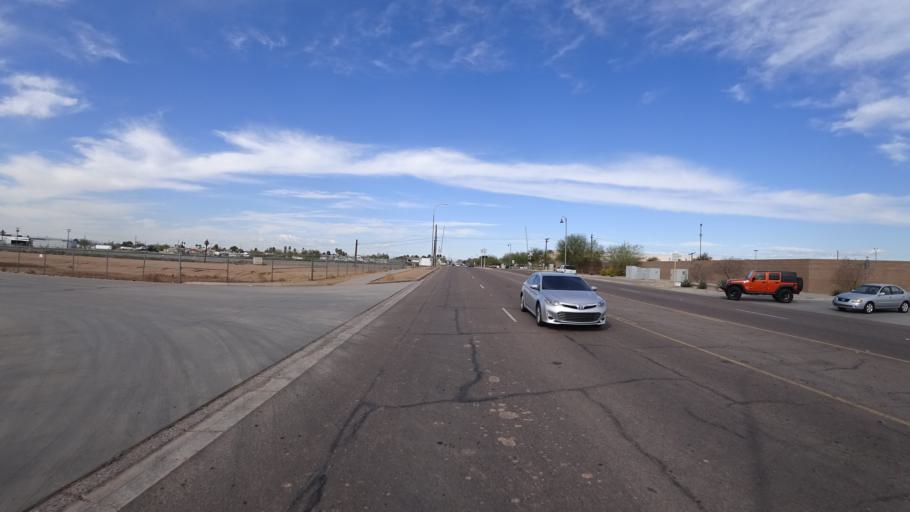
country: US
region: Arizona
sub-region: Maricopa County
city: Tolleson
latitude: 33.4425
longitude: -112.2552
